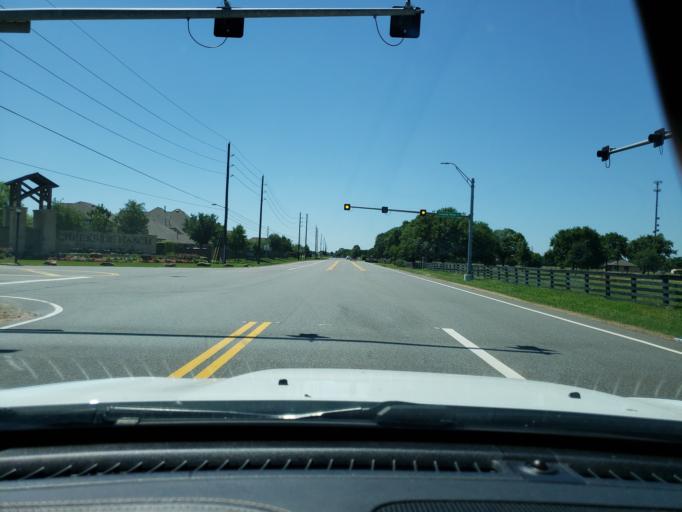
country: US
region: Texas
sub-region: Fort Bend County
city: Fulshear
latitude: 29.6676
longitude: -95.8381
